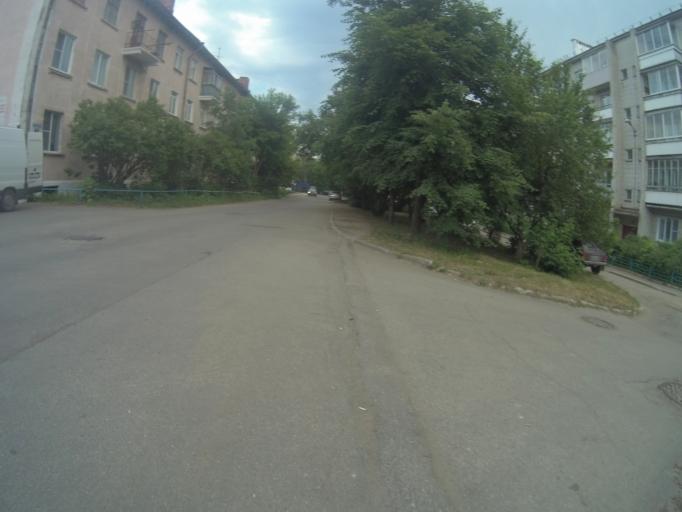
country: RU
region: Vladimir
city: Vladimir
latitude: 56.1397
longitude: 40.3949
